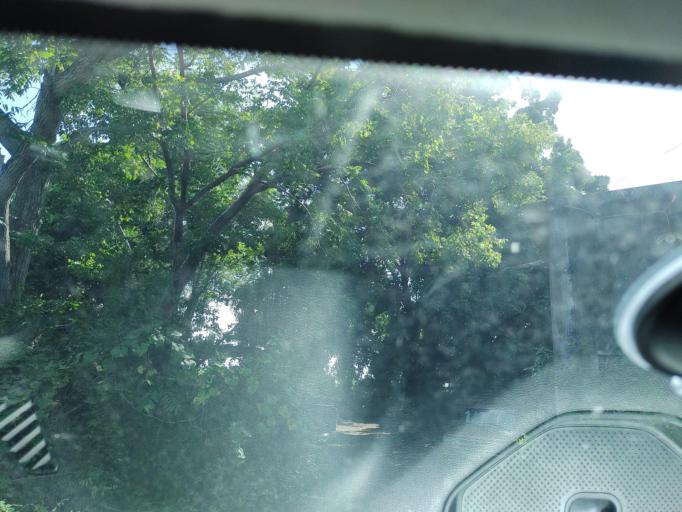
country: MX
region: Veracruz
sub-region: Martinez de la Torre
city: El Progreso
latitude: 20.1160
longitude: -97.0128
